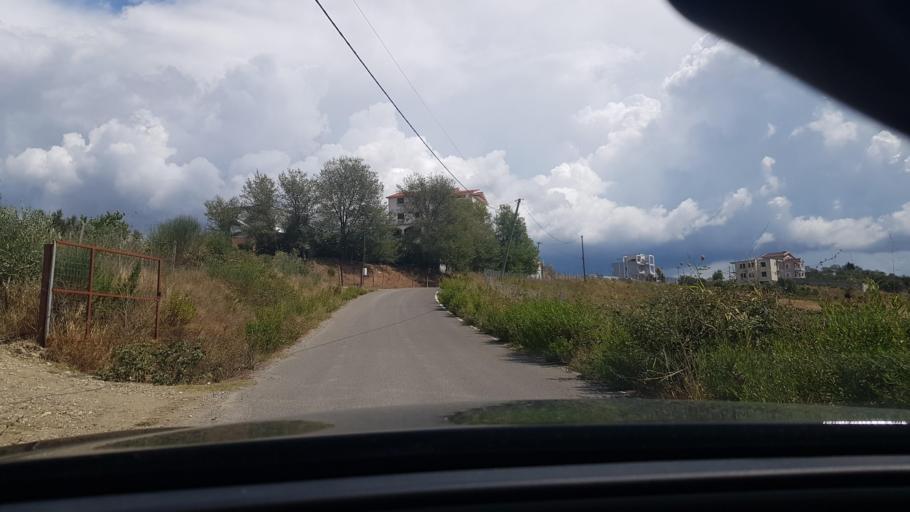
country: AL
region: Durres
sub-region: Rrethi i Durresit
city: Rrashbull
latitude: 41.2947
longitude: 19.5332
